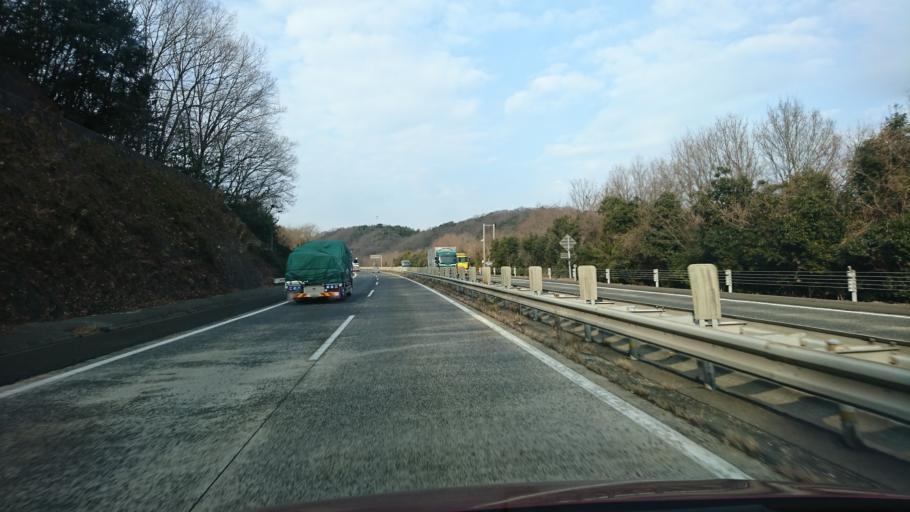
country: JP
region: Hyogo
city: Kariya
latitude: 34.7829
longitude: 134.2835
